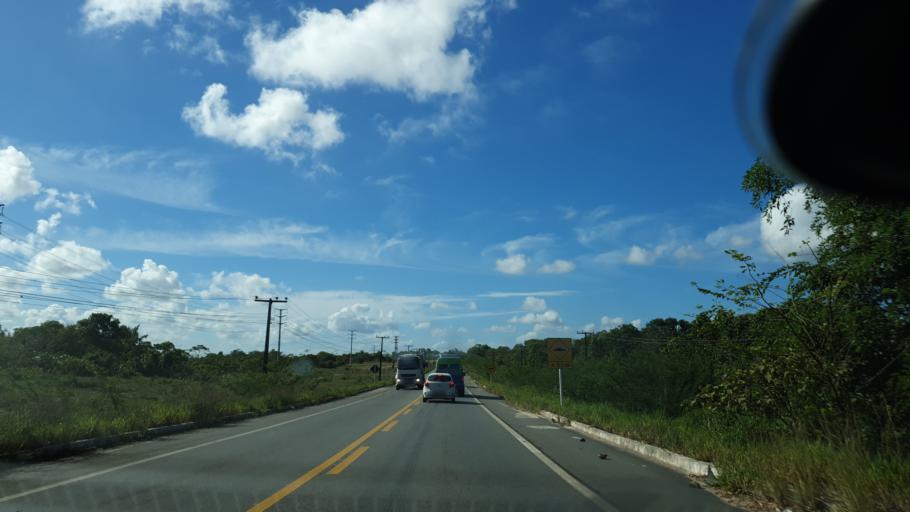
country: BR
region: Bahia
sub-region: Camacari
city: Camacari
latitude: -12.6883
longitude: -38.2282
